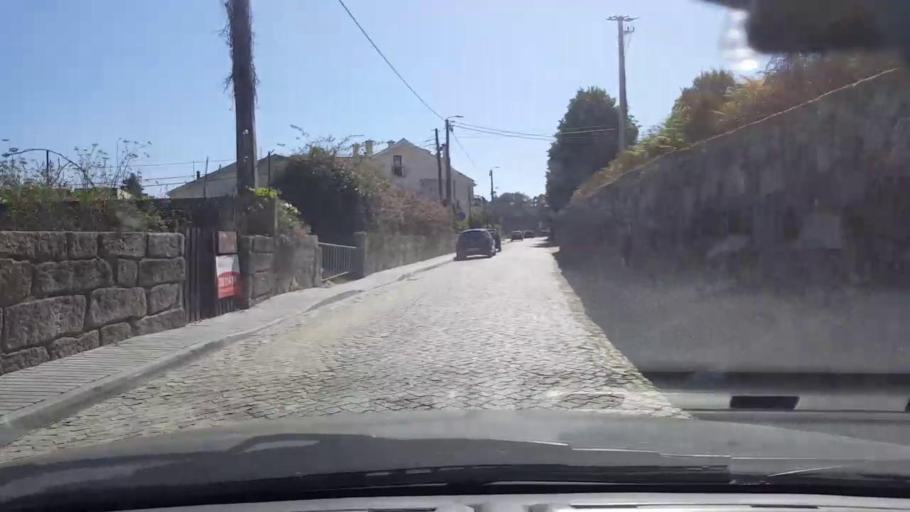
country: PT
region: Porto
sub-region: Vila do Conde
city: Arvore
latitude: 41.3094
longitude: -8.7184
